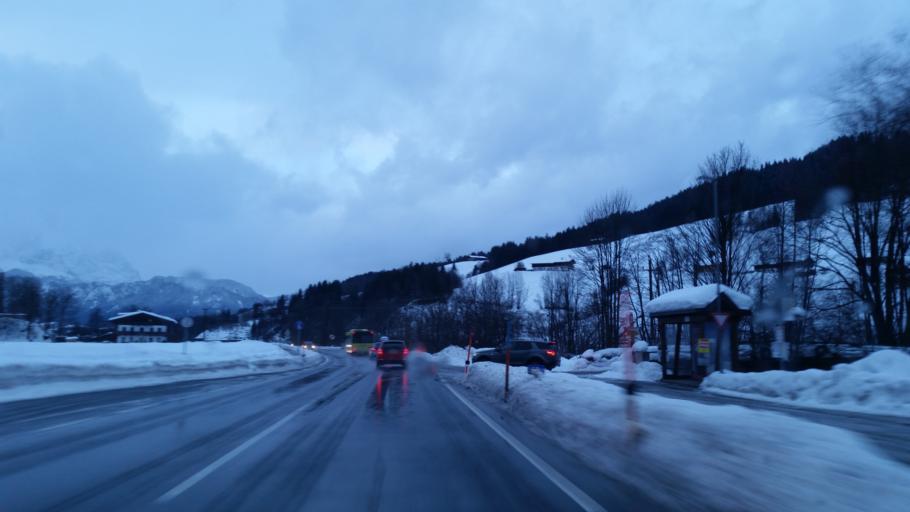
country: AT
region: Tyrol
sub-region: Politischer Bezirk Kitzbuhel
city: Fieberbrunn
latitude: 47.4994
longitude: 12.4879
